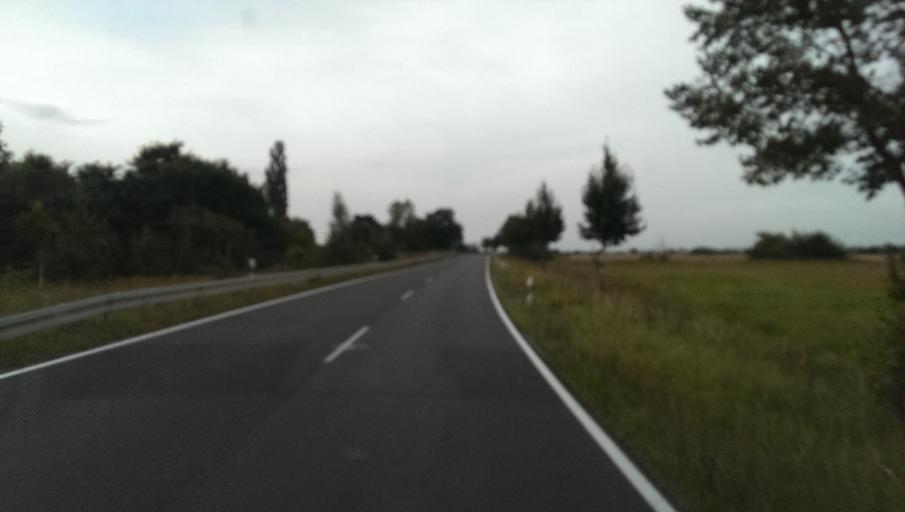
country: DE
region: Saxony-Anhalt
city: Kemberg
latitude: 51.7873
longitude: 12.6482
